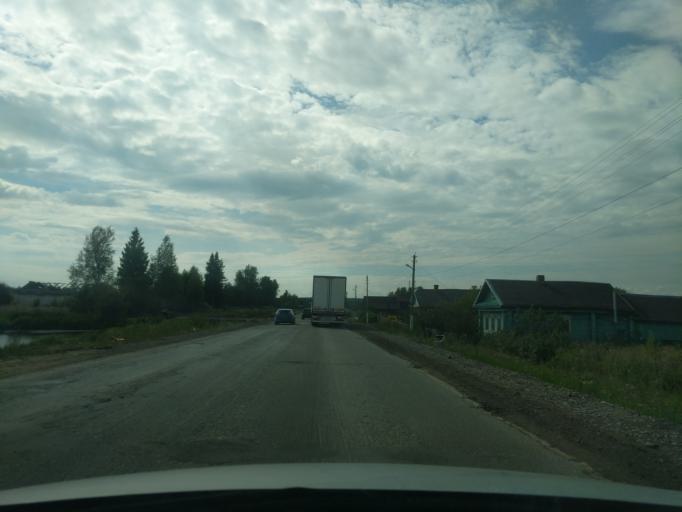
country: RU
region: Kostroma
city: Sudislavl'
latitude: 57.8612
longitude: 41.6174
